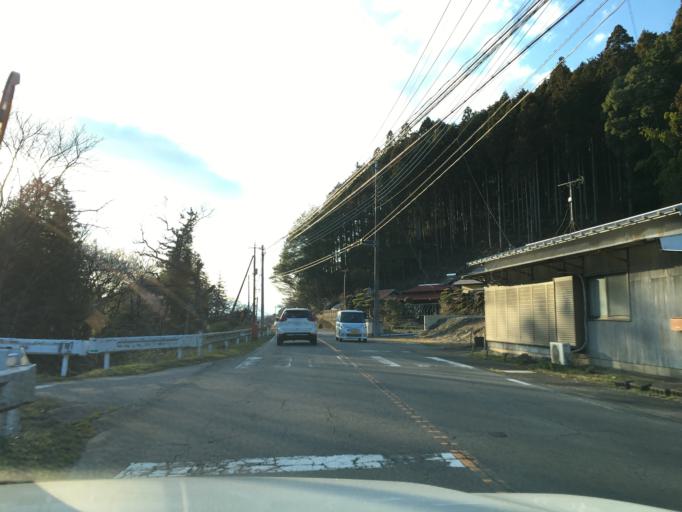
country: JP
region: Tochigi
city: Otawara
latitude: 36.8660
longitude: 140.1618
